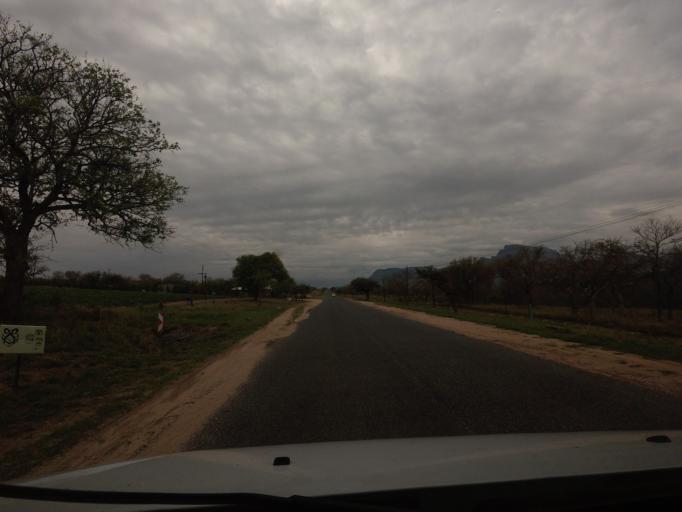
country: ZA
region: Limpopo
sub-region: Mopani District Municipality
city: Hoedspruit
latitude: -24.4565
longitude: 30.8662
